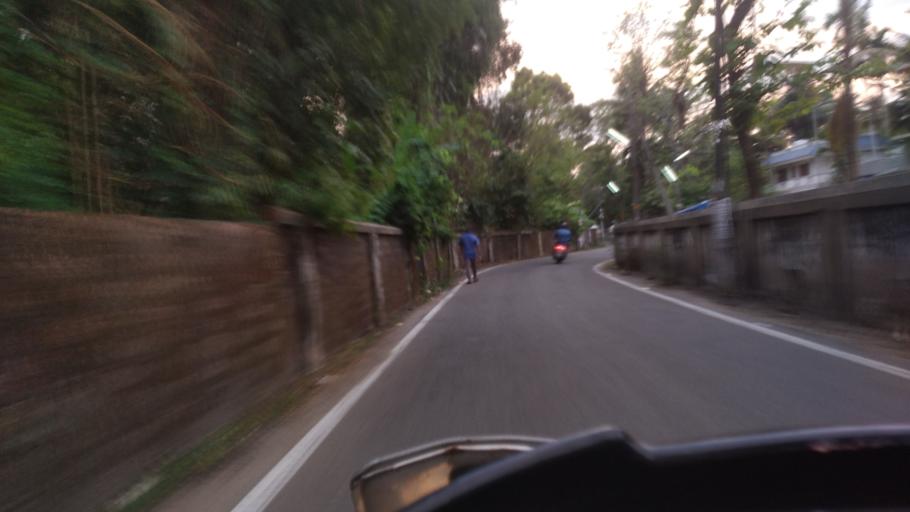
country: IN
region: Kerala
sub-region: Thrissur District
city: Kodungallur
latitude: 10.1479
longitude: 76.2174
